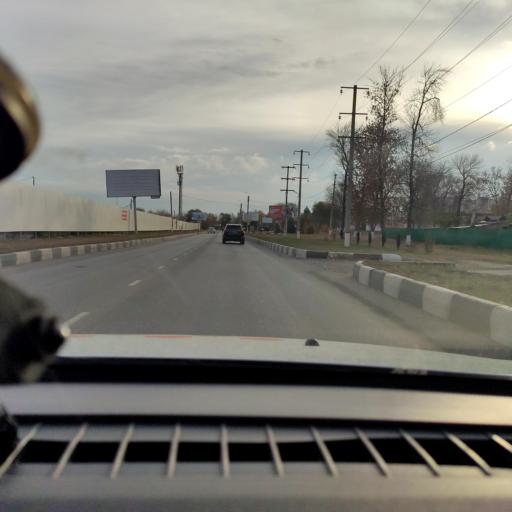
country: RU
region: Samara
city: Novokuybyshevsk
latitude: 53.1167
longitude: 49.9379
